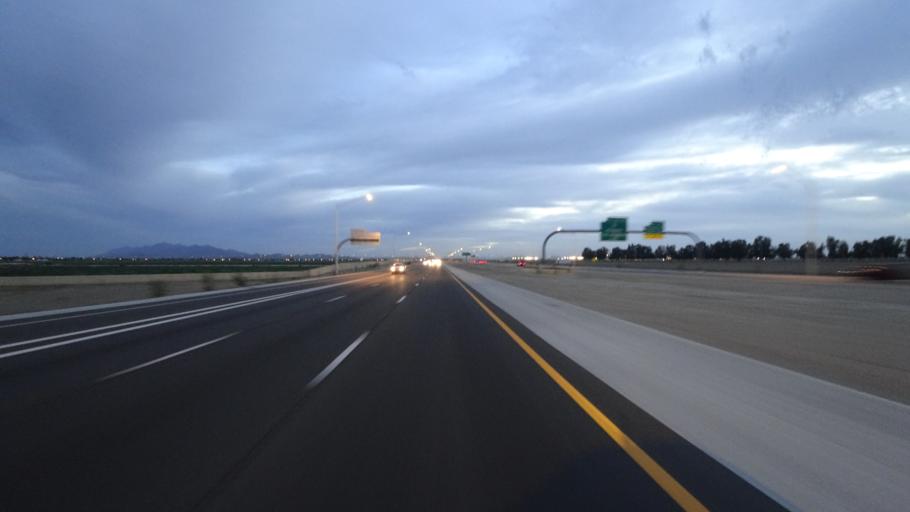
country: US
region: Arizona
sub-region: Maricopa County
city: Litchfield Park
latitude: 33.4888
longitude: -112.4214
